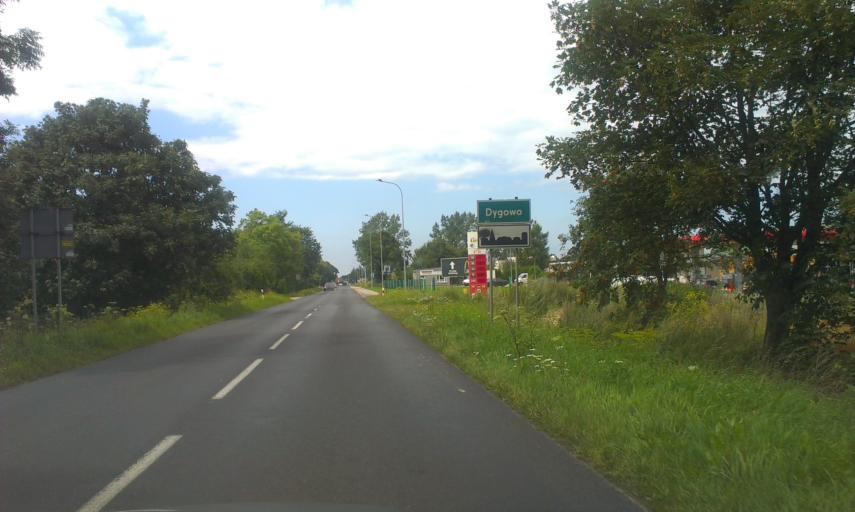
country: PL
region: West Pomeranian Voivodeship
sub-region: Powiat kolobrzeski
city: Dygowo
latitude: 54.1265
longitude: 15.7283
